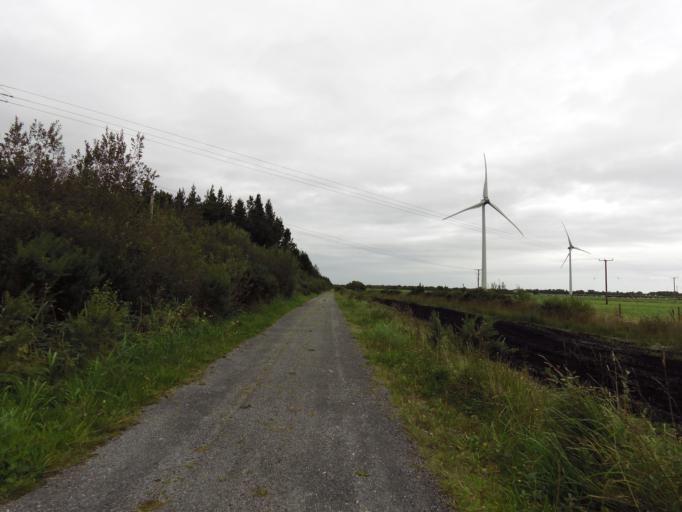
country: IE
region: Leinster
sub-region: Uibh Fhaili
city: Ferbane
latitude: 53.2315
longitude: -7.7731
